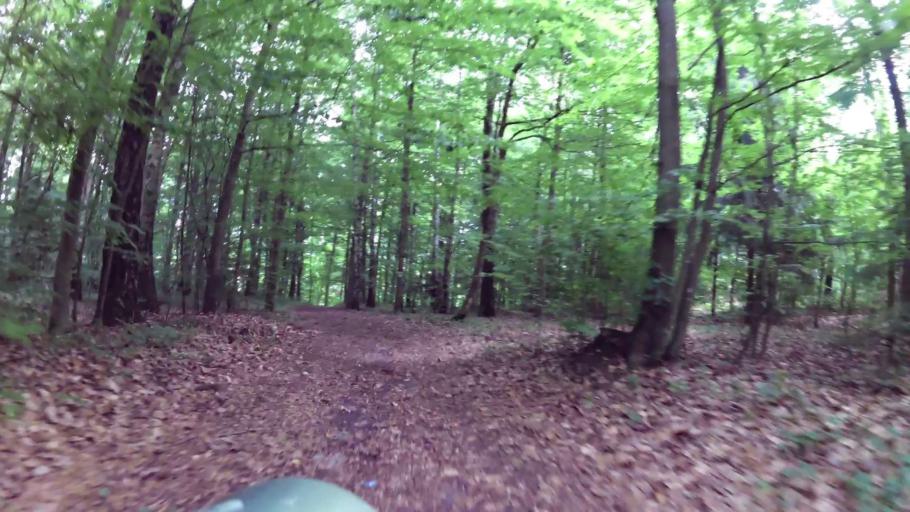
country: PL
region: West Pomeranian Voivodeship
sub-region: Powiat szczecinecki
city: Bialy Bor
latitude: 53.9003
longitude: 16.8271
